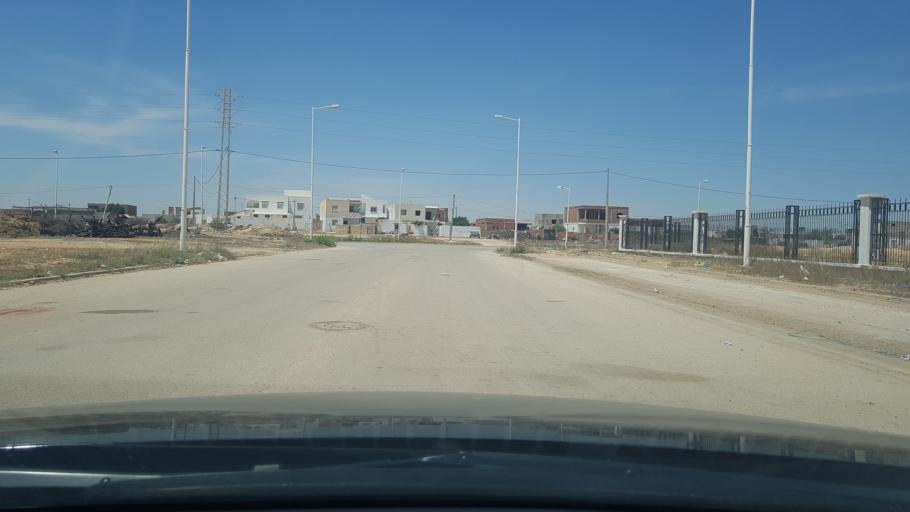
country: TN
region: Safaqis
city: Al Qarmadah
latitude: 34.8357
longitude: 10.7485
